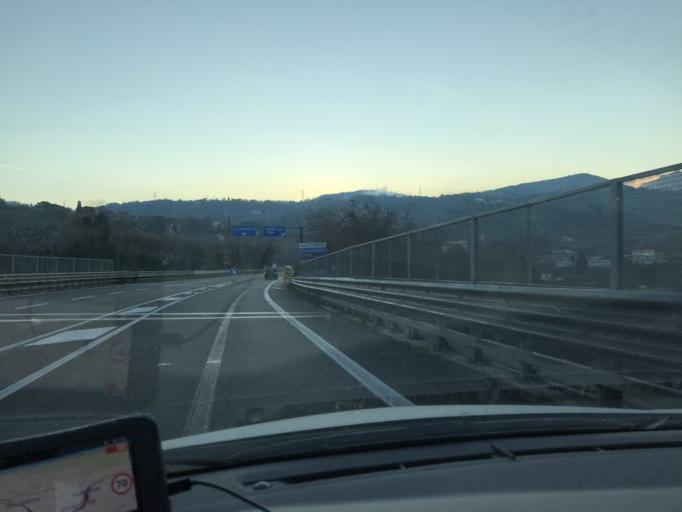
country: IT
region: Umbria
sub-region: Provincia di Terni
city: Terni
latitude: 42.5826
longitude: 12.6786
